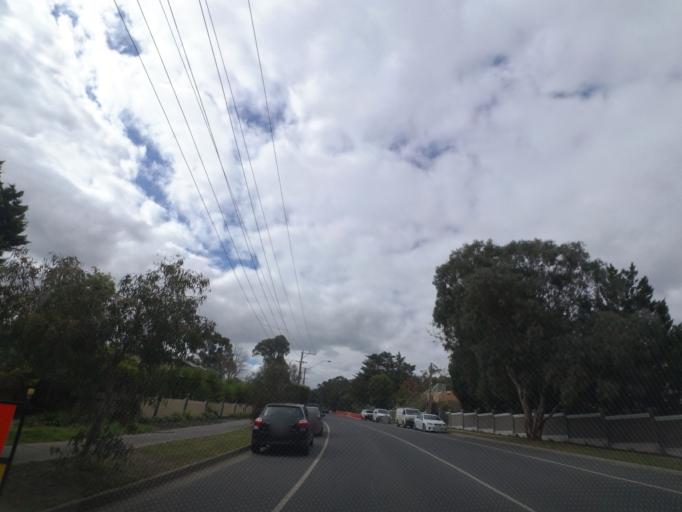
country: AU
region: Victoria
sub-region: Nillumbik
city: Diamond Creek
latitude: -37.6681
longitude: 145.1632
